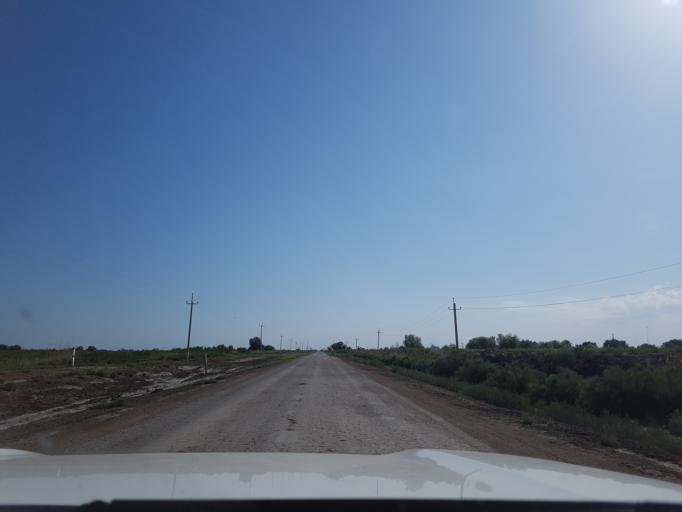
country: TM
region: Dasoguz
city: Koeneuergench
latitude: 42.0711
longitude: 58.8602
